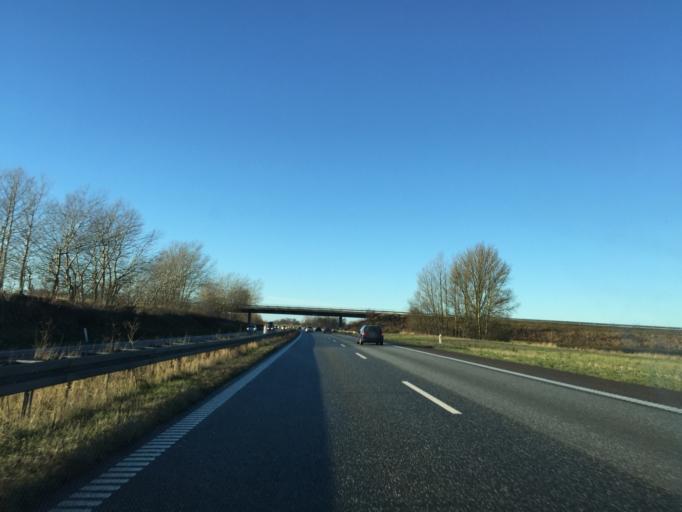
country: DK
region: South Denmark
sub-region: Nyborg Kommune
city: Ullerslev
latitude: 55.3433
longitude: 10.6715
